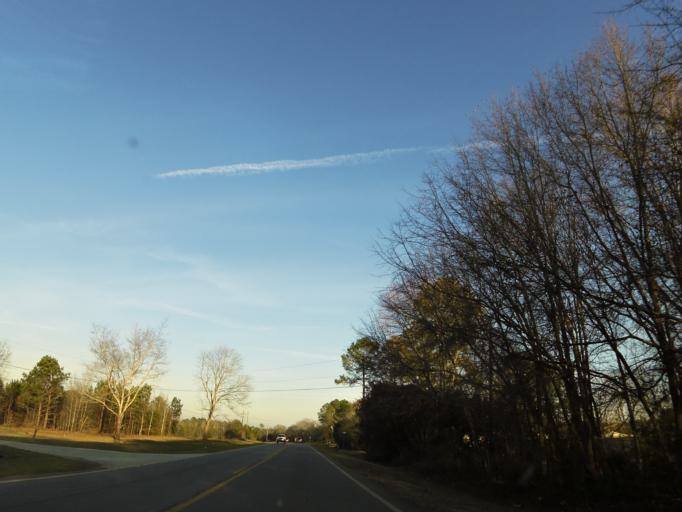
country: US
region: Georgia
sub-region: Sumter County
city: Americus
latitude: 32.0558
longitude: -84.2826
